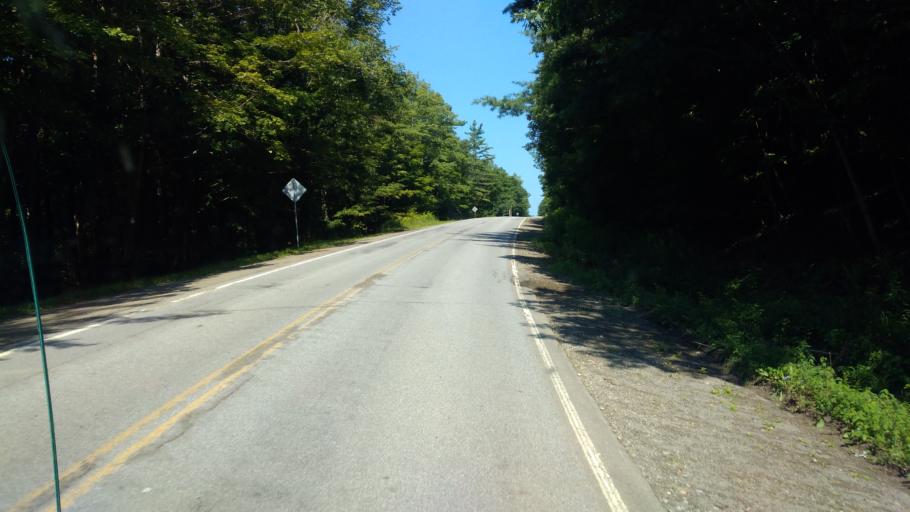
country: US
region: New York
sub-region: Allegany County
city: Bolivar
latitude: 42.0891
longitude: -78.1641
